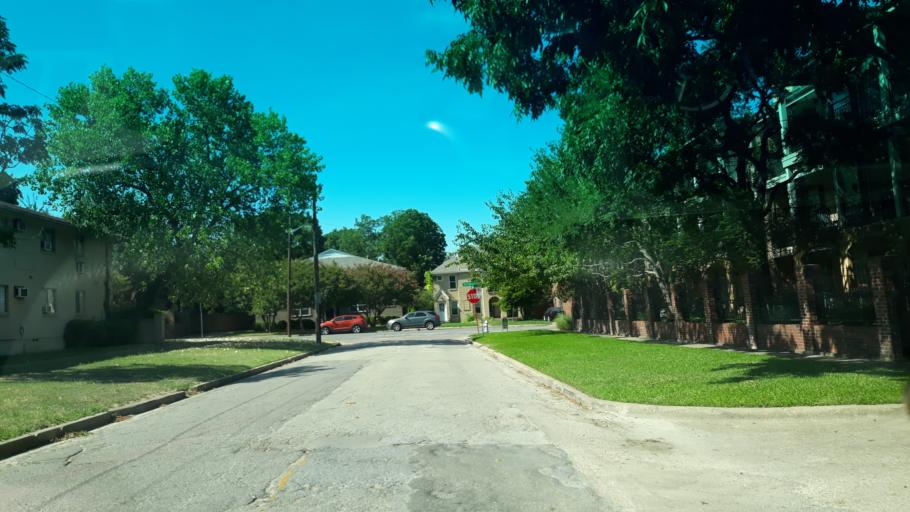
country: US
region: Texas
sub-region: Dallas County
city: Highland Park
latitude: 32.8157
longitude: -96.7552
